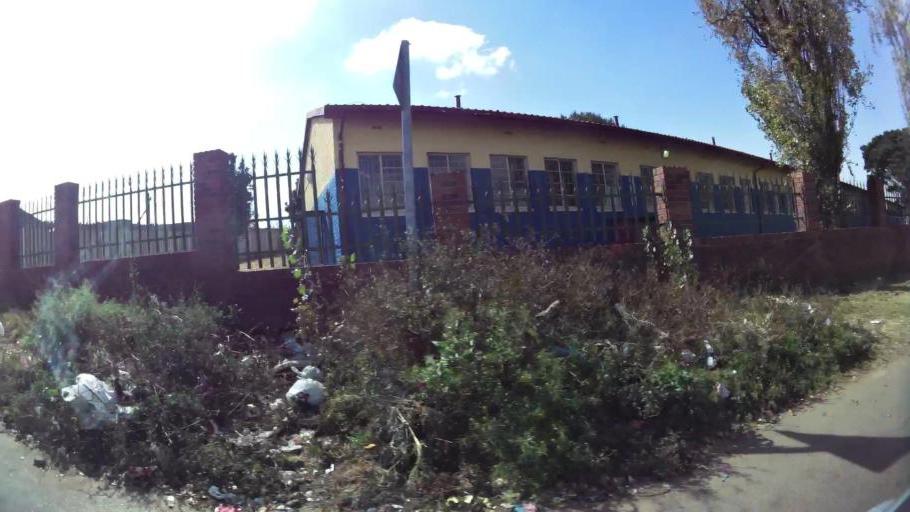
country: ZA
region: Gauteng
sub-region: City of Johannesburg Metropolitan Municipality
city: Soweto
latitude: -26.2252
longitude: 27.8933
